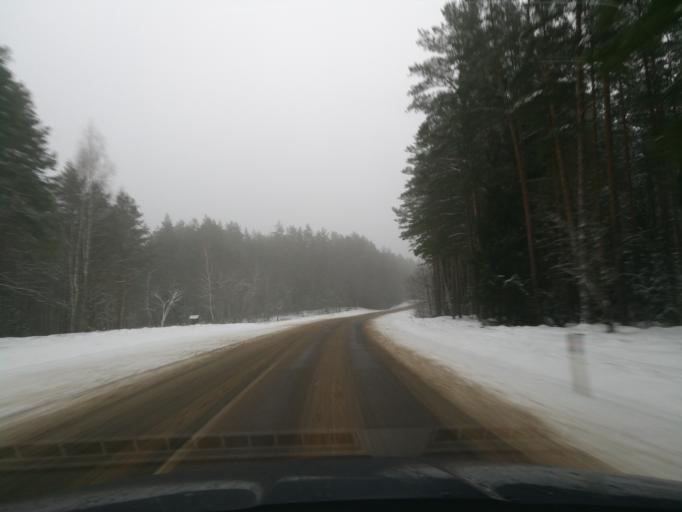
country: LT
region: Utenos apskritis
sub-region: Anyksciai
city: Anyksciai
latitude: 55.4600
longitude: 25.0429
